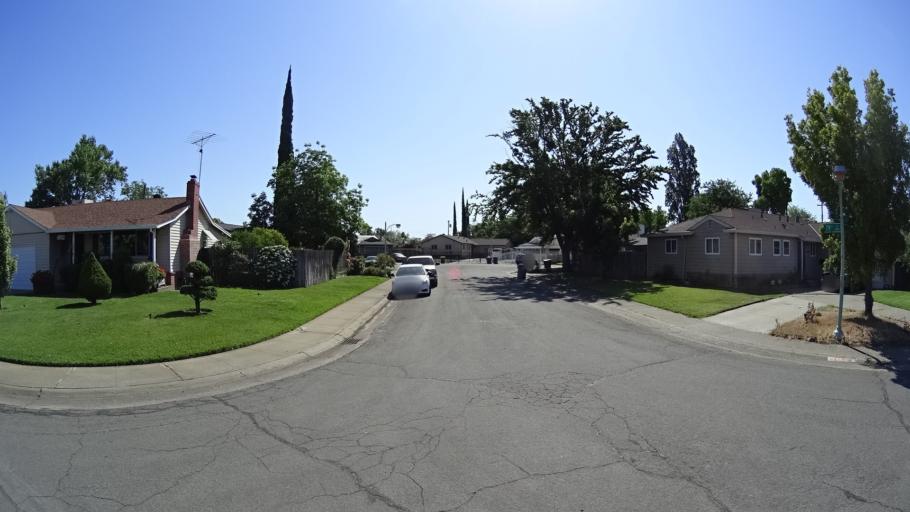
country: US
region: California
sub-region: Sacramento County
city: Florin
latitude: 38.5307
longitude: -121.4126
